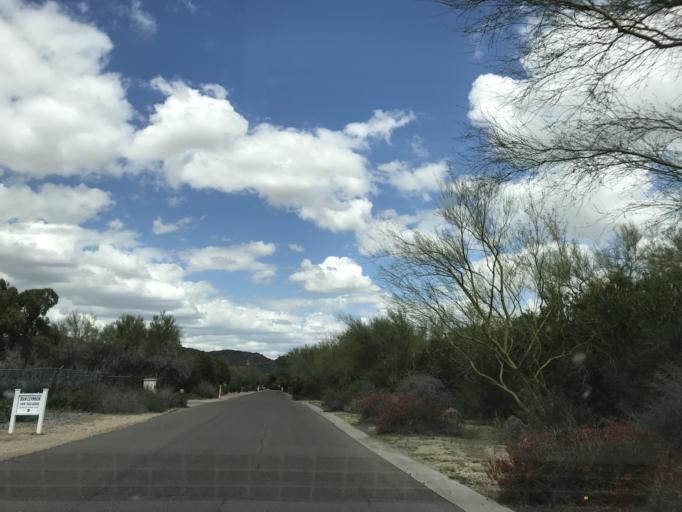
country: US
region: Arizona
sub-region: Maricopa County
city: Paradise Valley
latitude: 33.5185
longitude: -111.9454
